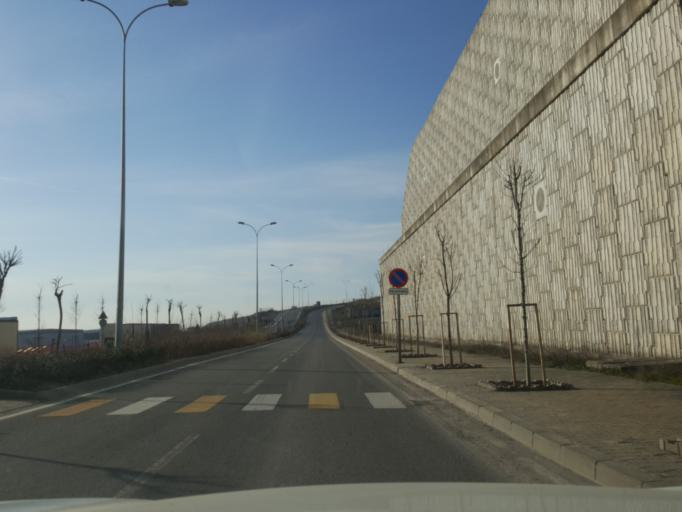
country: TR
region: Kocaeli
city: Tavsanli
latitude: 40.8329
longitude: 29.5536
